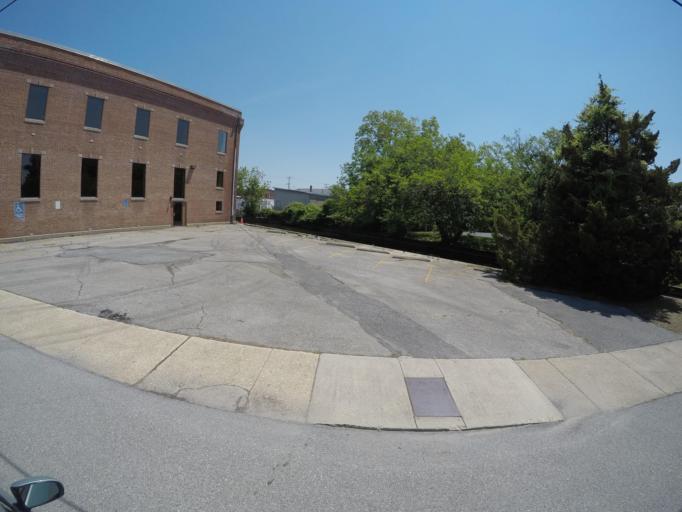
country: US
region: Delaware
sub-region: Sussex County
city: Milford
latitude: 38.9123
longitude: -75.4307
